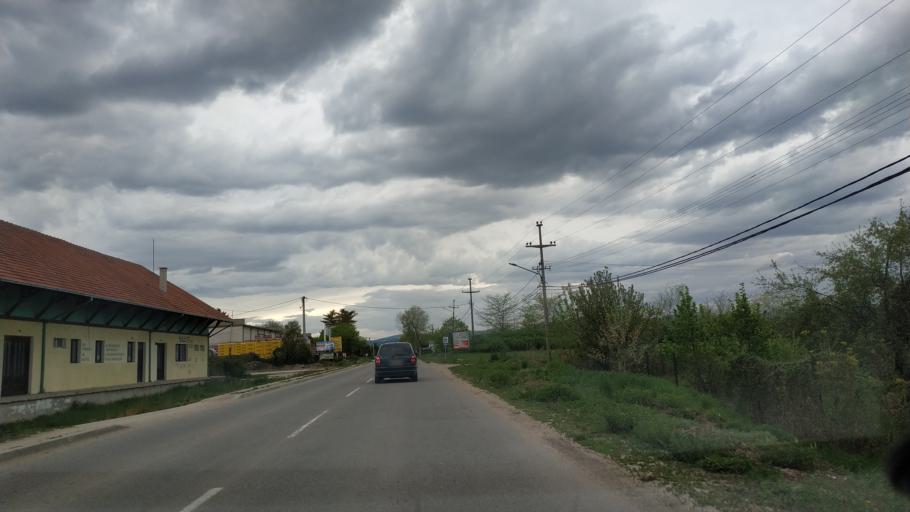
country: RS
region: Central Serbia
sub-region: Zajecarski Okrug
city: Soko Banja
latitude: 43.6515
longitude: 21.8515
